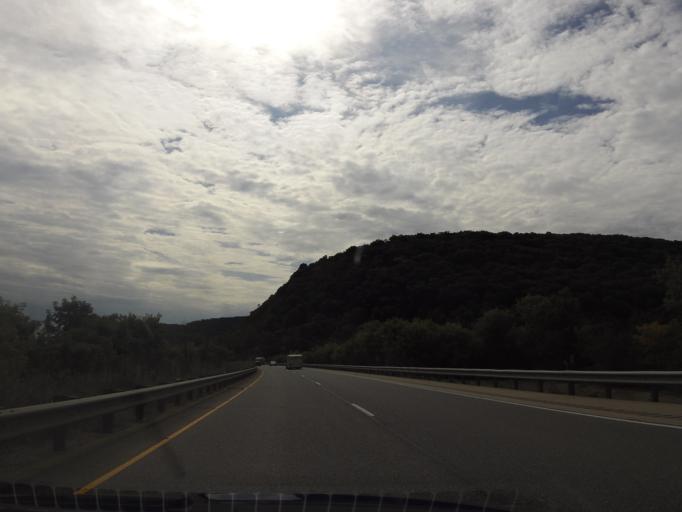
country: US
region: Wisconsin
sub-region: Trempealeau County
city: Trempealeau
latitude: 43.9289
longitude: -91.4130
